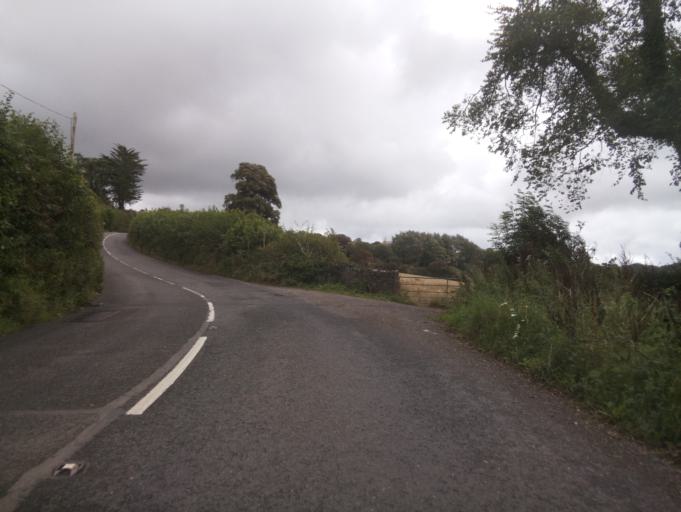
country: GB
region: England
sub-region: Devon
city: Kingsbridge
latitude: 50.2725
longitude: -3.7087
